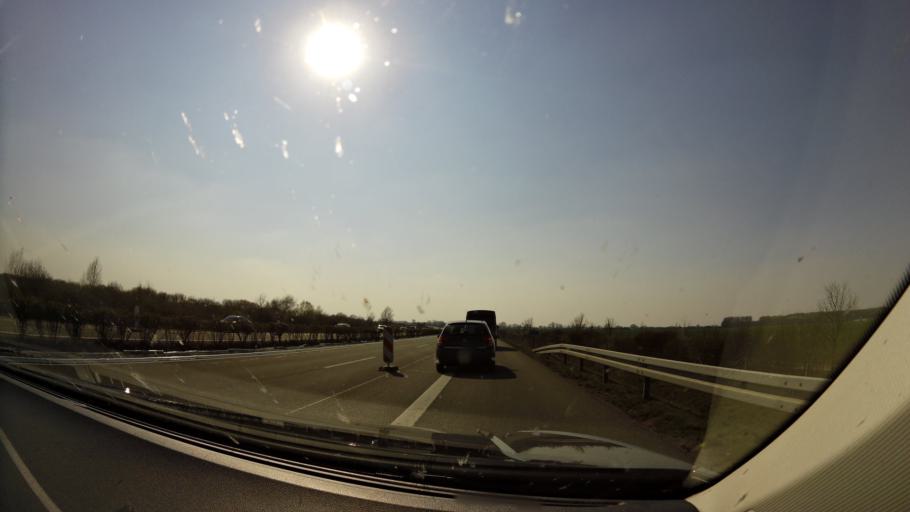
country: DE
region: Mecklenburg-Vorpommern
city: Grimmen
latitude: 54.0873
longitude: 12.9573
